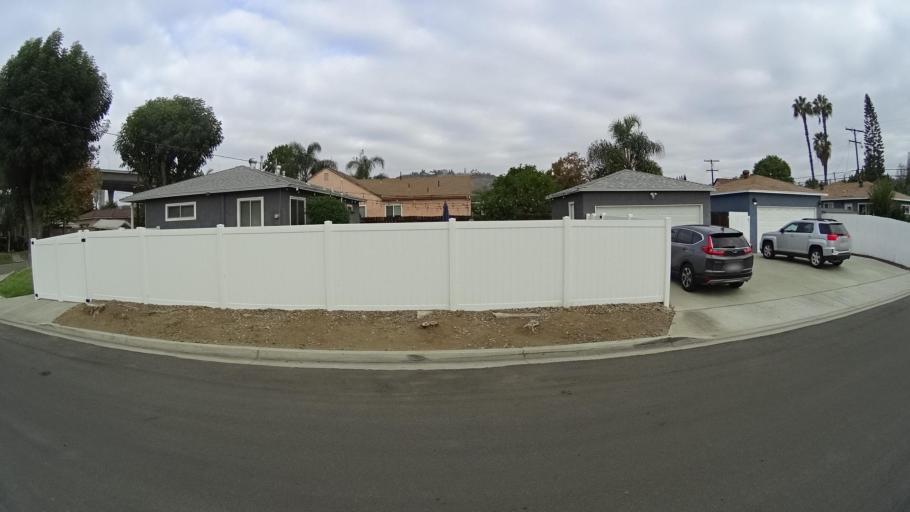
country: US
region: California
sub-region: San Diego County
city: Lemon Grove
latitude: 32.7435
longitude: -117.0153
